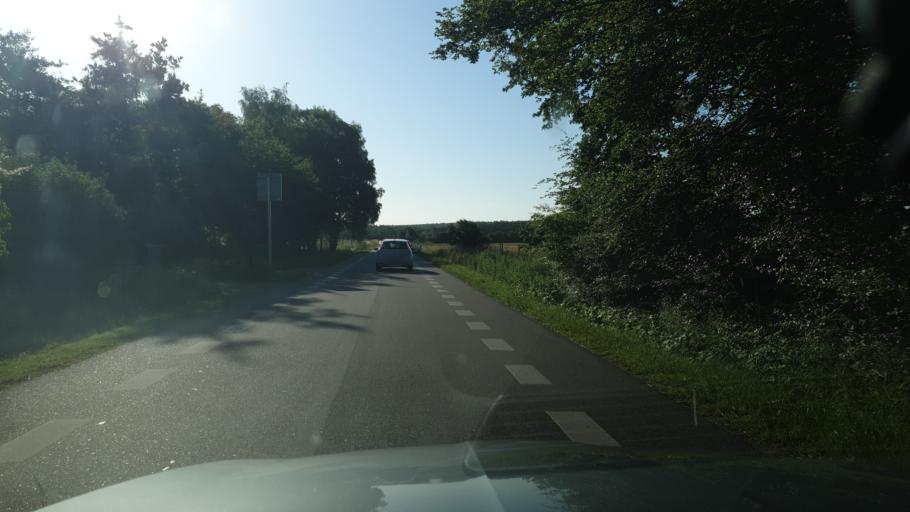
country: DK
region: Zealand
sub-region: Soro Kommune
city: Frederiksberg
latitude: 55.4089
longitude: 11.6101
